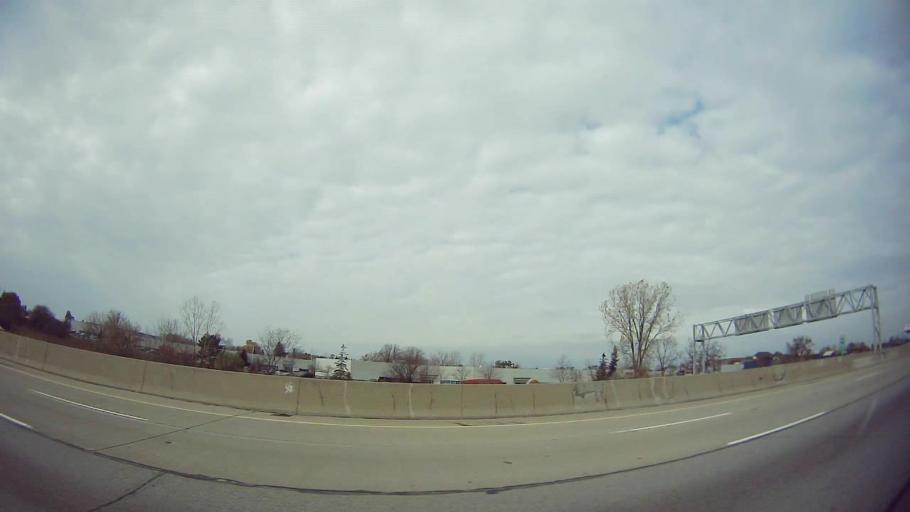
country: US
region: Michigan
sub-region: Oakland County
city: Auburn Hills
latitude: 42.6691
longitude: -83.2410
